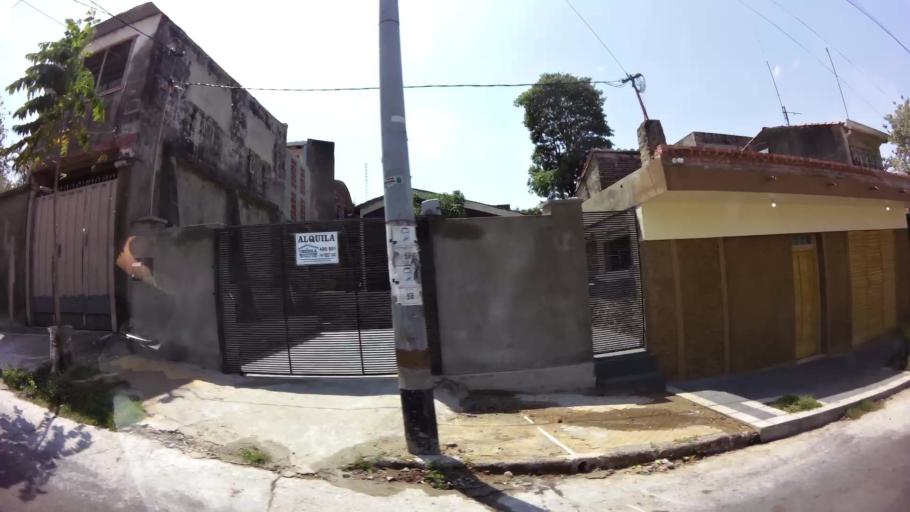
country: PY
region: Presidente Hayes
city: Nanawa
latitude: -25.2807
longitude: -57.6485
